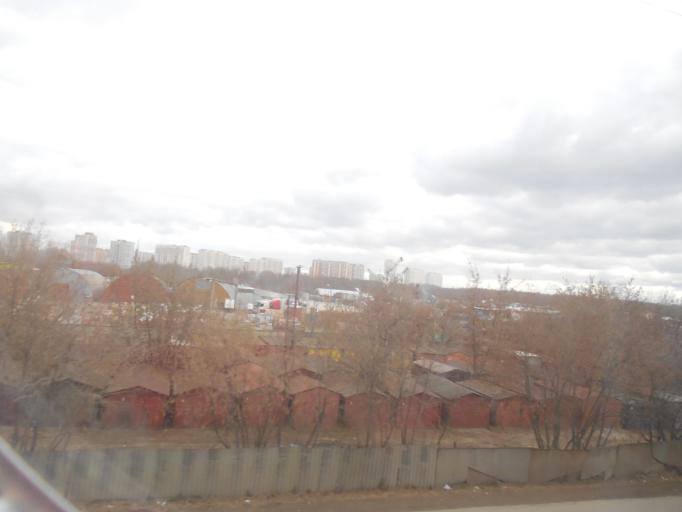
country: RU
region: Moskovskaya
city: Lyubertsy
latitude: 55.6788
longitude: 37.9042
